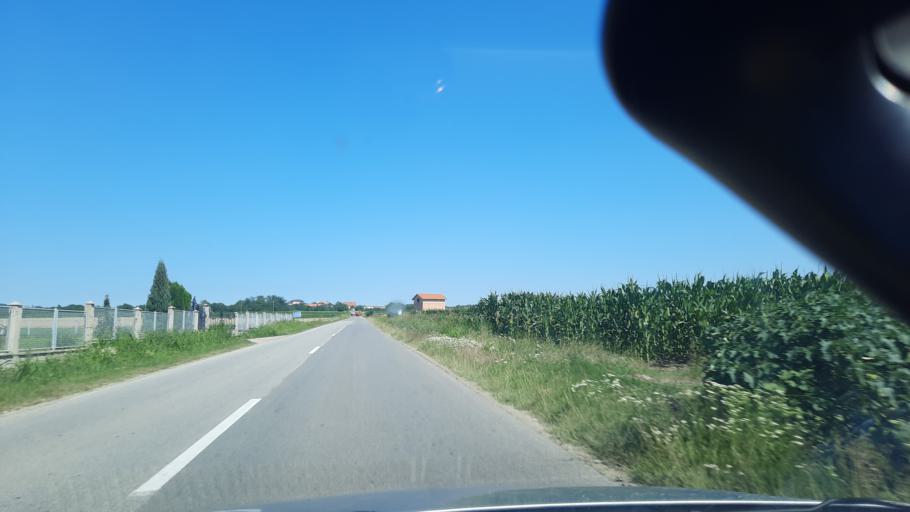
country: RS
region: Central Serbia
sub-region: Branicevski Okrug
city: Malo Crnice
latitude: 44.5750
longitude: 21.3490
